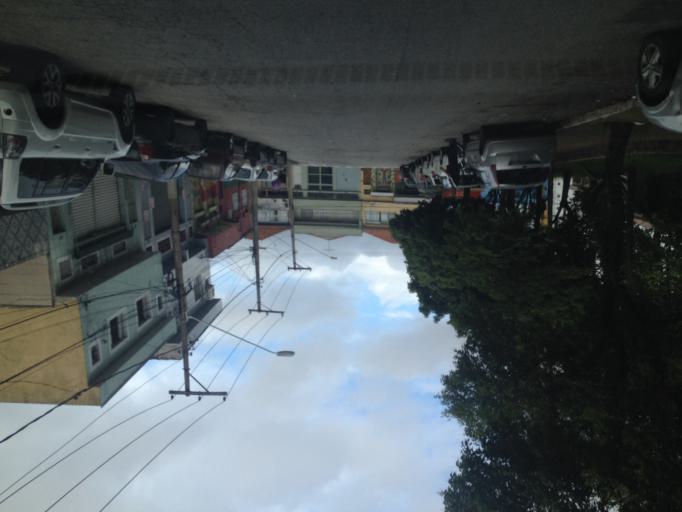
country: BR
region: Sao Paulo
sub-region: Sao Caetano Do Sul
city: Sao Caetano do Sul
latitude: -23.5694
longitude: -46.5669
